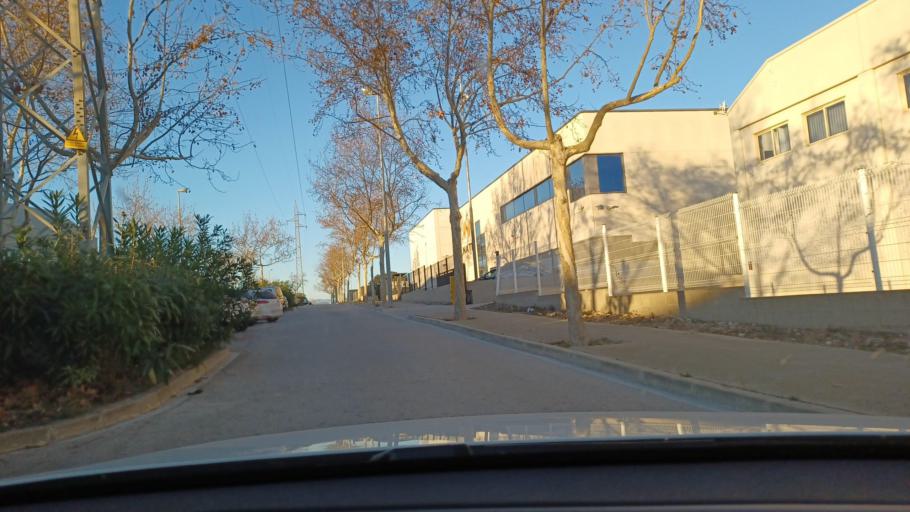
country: ES
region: Catalonia
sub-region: Provincia de Tarragona
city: Amposta
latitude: 40.7025
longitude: 0.5617
